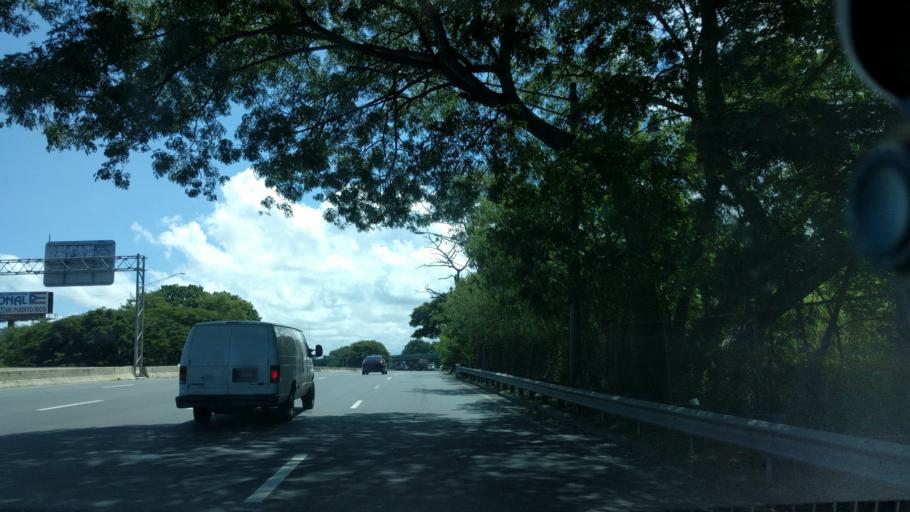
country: PR
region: San Juan
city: San Juan
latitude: 18.4419
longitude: -66.0749
